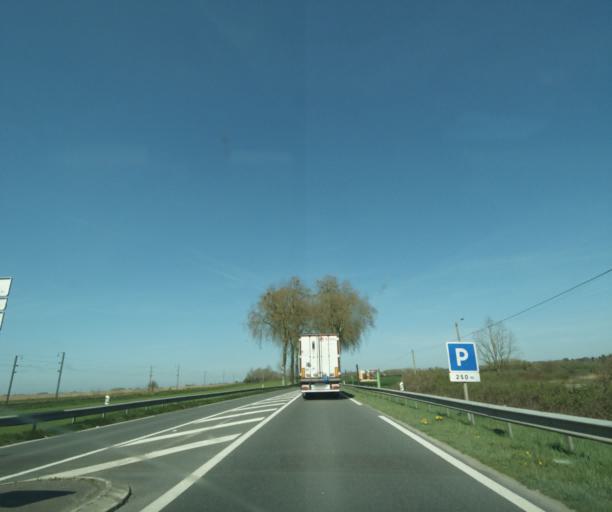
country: FR
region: Bourgogne
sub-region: Departement de la Nievre
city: Chantenay-Saint-Imbert
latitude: 46.7043
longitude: 3.2004
